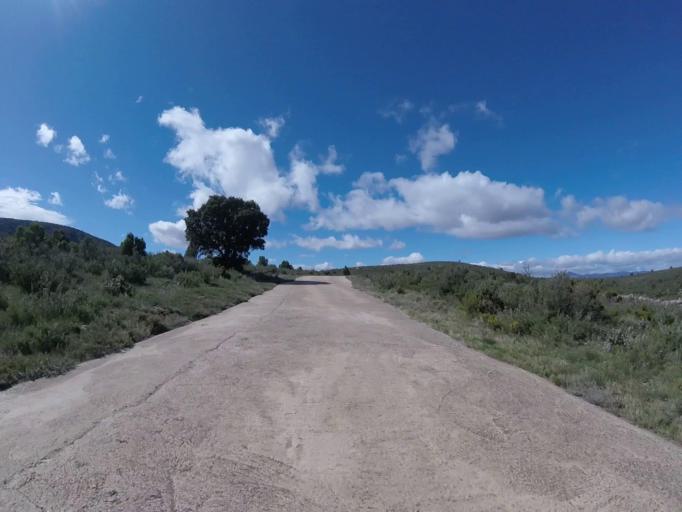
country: ES
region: Valencia
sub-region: Provincia de Castello
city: Culla
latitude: 40.3128
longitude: -0.0972
